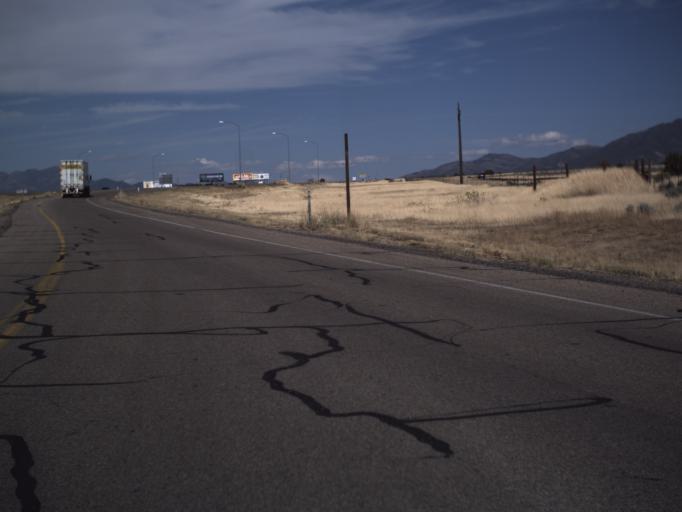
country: US
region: Utah
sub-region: Millard County
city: Fillmore
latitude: 38.9922
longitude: -112.3222
